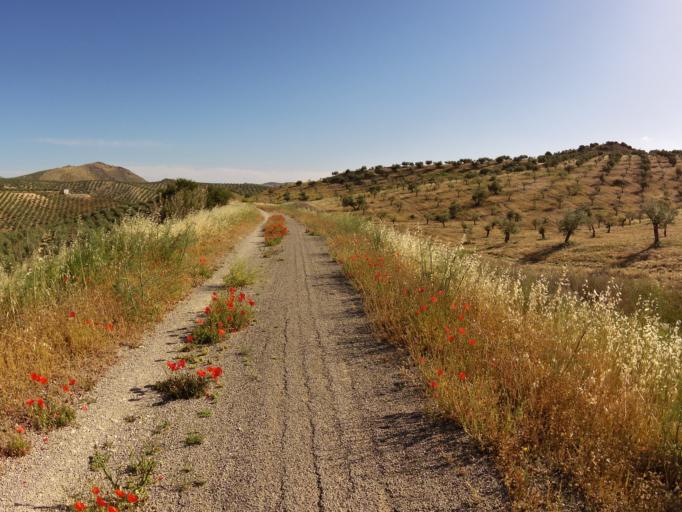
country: ES
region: Andalusia
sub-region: Province of Cordoba
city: Fuente-Tojar
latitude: 37.5815
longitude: -4.1770
